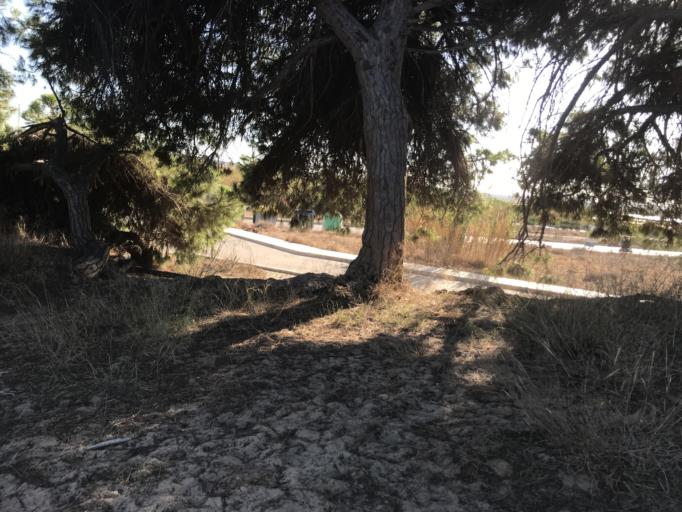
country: ES
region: Valencia
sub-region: Provincia de Alicante
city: Torrevieja
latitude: 38.0314
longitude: -0.6569
